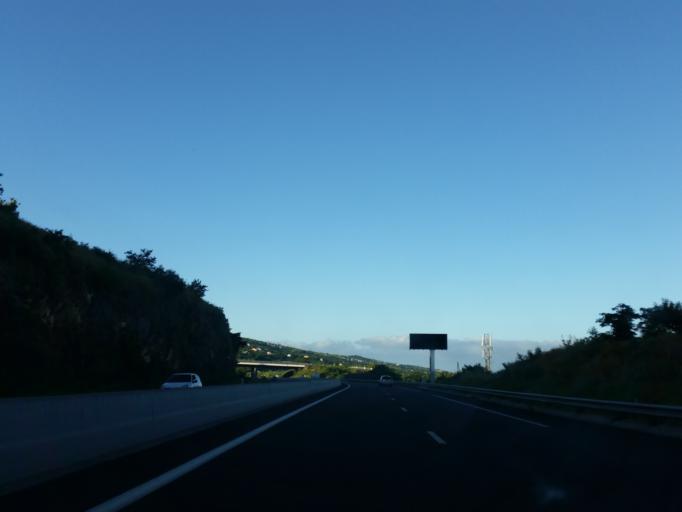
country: RE
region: Reunion
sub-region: Reunion
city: Saint-Leu
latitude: -21.1575
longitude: 55.2953
